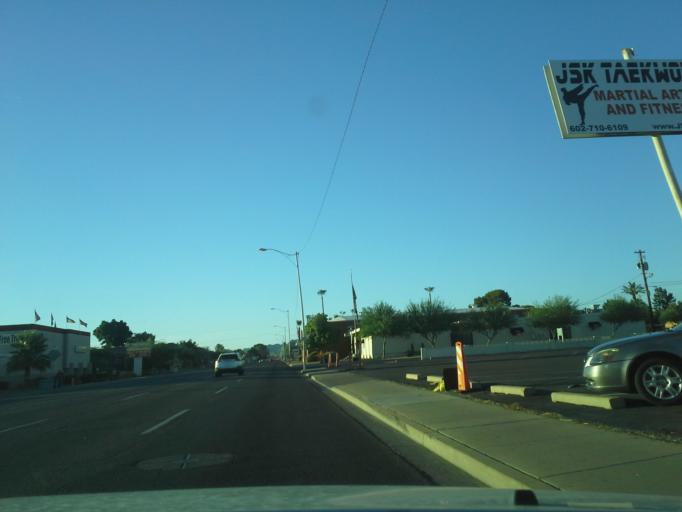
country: US
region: Arizona
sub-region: Maricopa County
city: Phoenix
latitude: 33.4834
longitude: -112.0301
